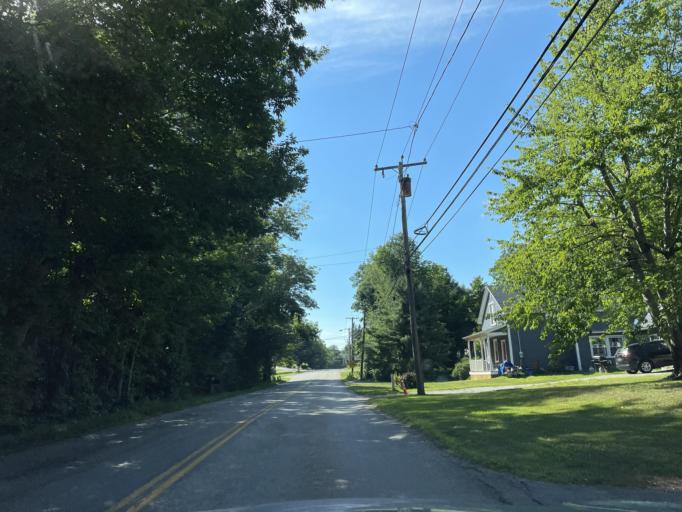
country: US
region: Massachusetts
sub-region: Worcester County
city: Charlton
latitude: 42.1320
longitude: -71.9352
